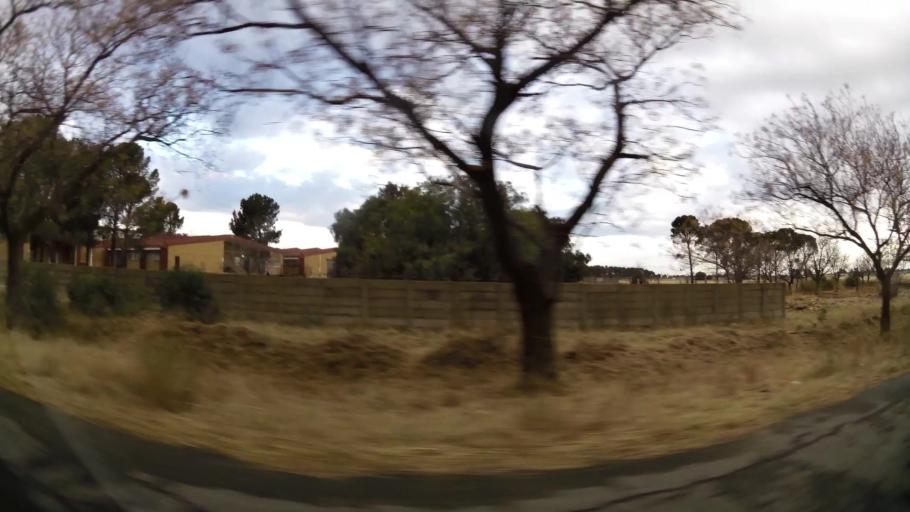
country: ZA
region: Orange Free State
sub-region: Lejweleputswa District Municipality
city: Welkom
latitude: -27.9621
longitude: 26.7131
